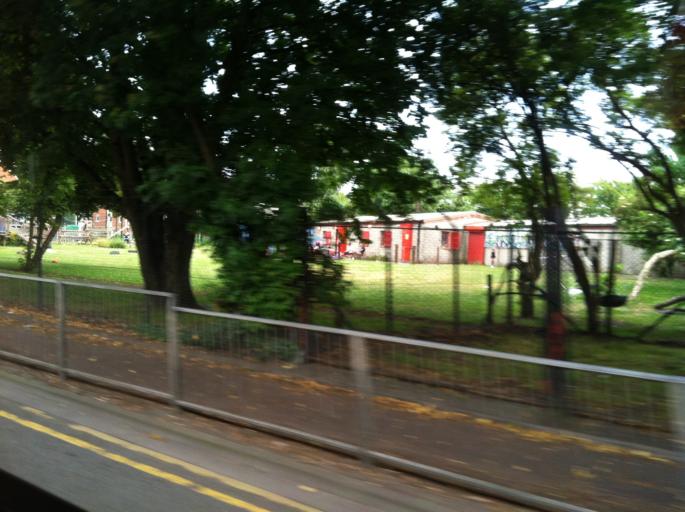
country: GB
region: Wales
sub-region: Cardiff
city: Cardiff
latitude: 51.4629
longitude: -3.1829
